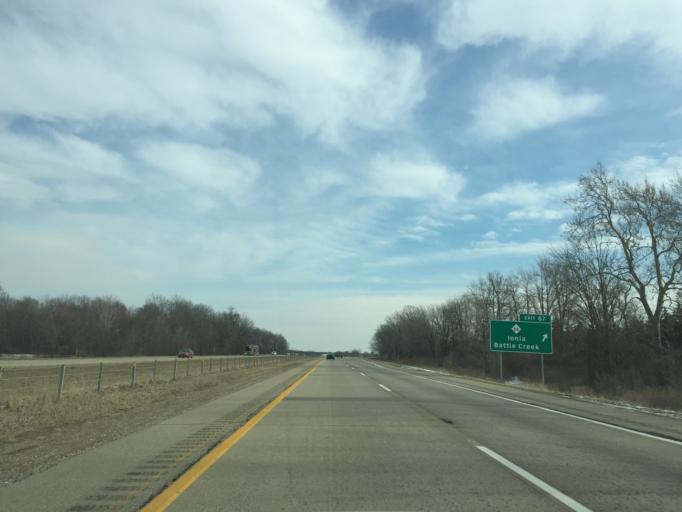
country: US
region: Michigan
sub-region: Ionia County
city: Lake Odessa
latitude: 42.8791
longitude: -85.0851
